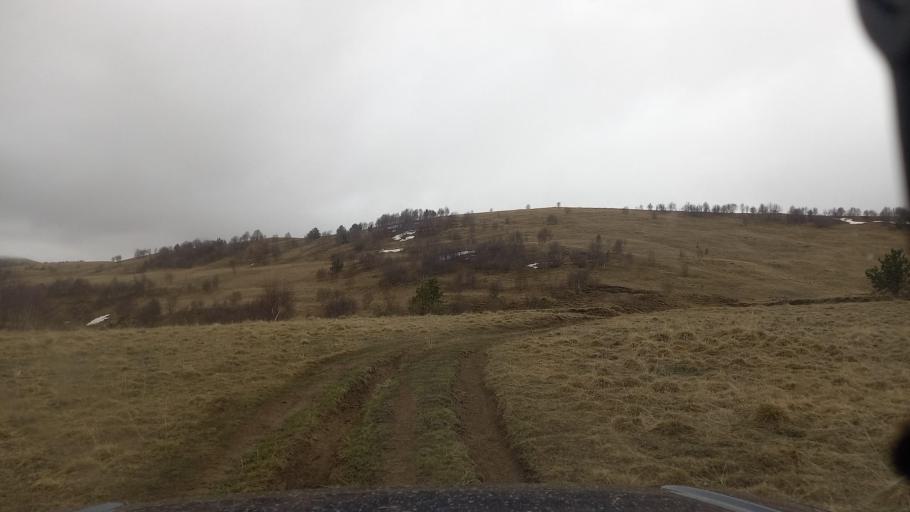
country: RU
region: Kabardino-Balkariya
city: Terskol
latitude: 43.5235
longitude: 42.4269
